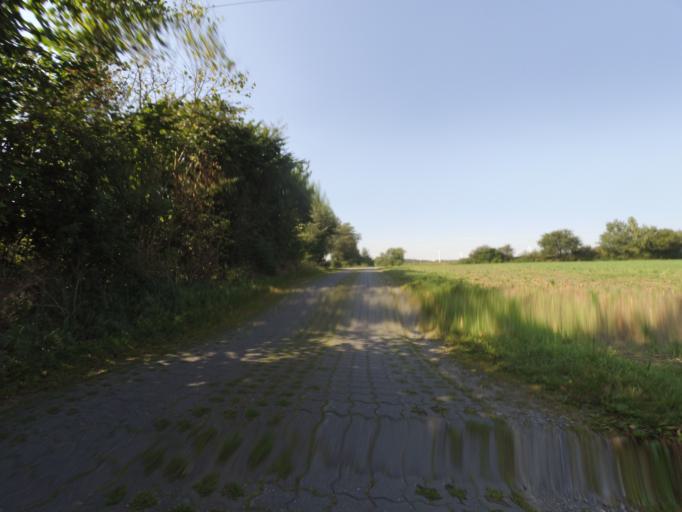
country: DE
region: North Rhine-Westphalia
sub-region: Regierungsbezirk Munster
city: Heek
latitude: 52.0904
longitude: 7.0905
